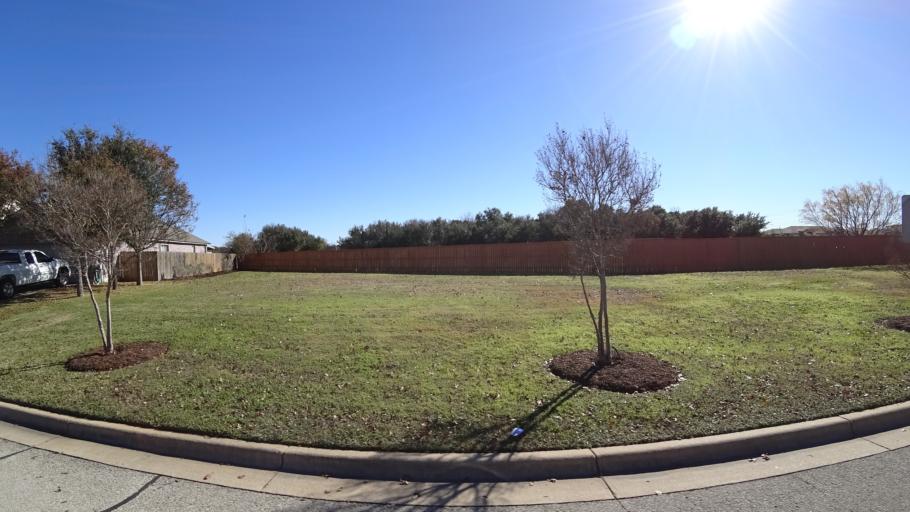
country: US
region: Texas
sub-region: Williamson County
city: Cedar Park
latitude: 30.5364
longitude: -97.8469
